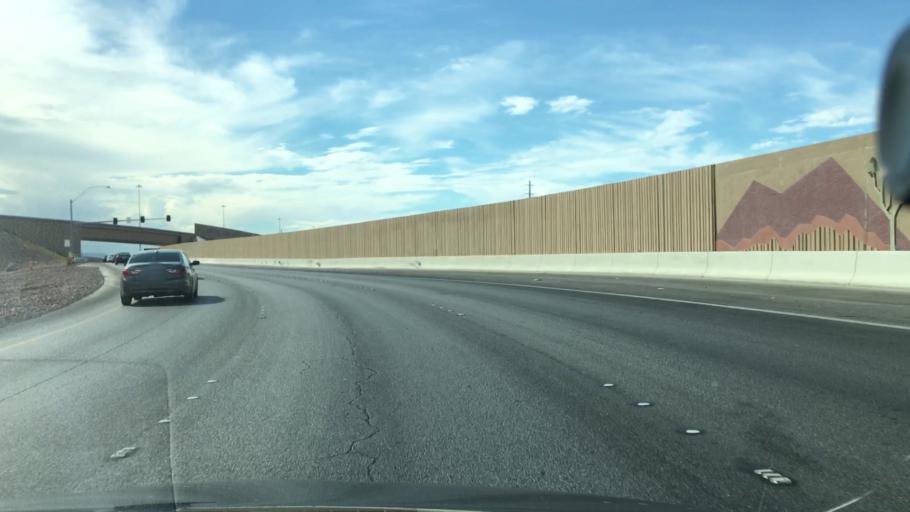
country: US
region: Nevada
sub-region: Clark County
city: Whitney
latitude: 36.0651
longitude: -115.0309
